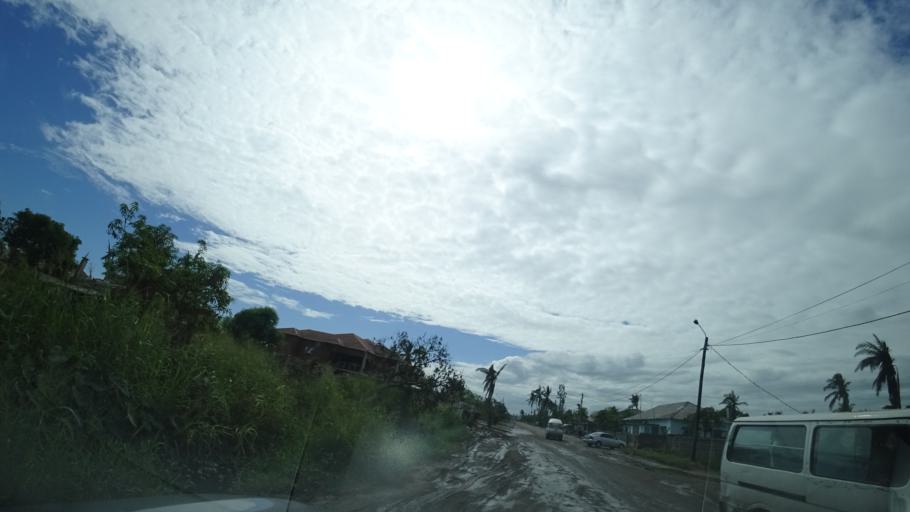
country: MZ
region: Sofala
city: Beira
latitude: -19.7641
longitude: 34.8664
